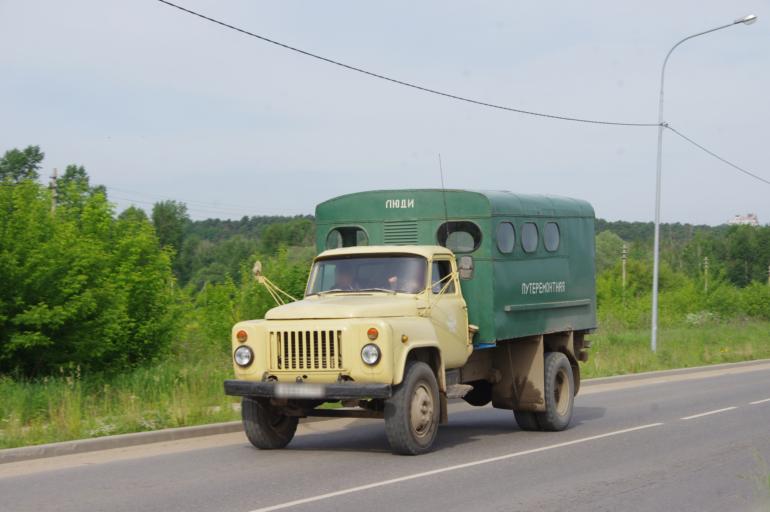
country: RU
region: Tula
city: Aleksin
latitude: 54.5162
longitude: 37.0713
